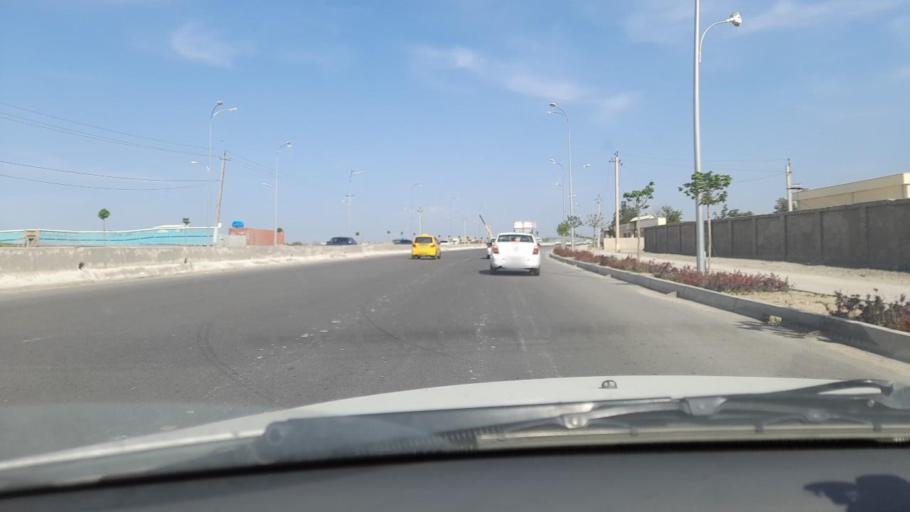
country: UZ
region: Samarqand
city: Samarqand
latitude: 39.7115
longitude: 66.9749
